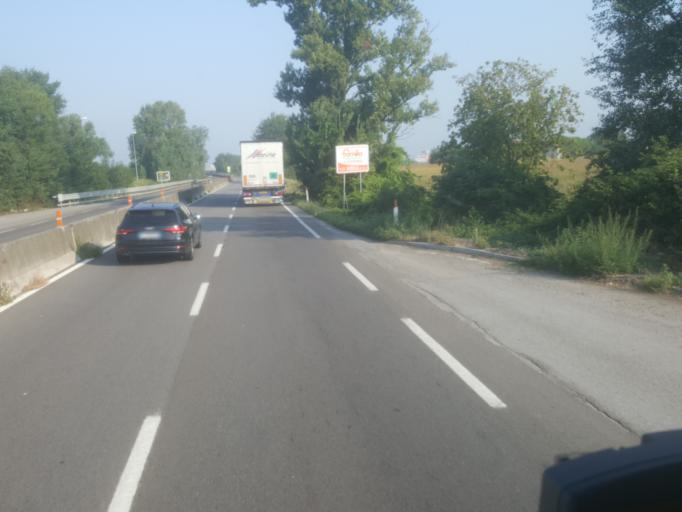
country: IT
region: Emilia-Romagna
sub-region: Provincia di Ravenna
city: Ravenna
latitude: 44.4157
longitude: 12.1691
